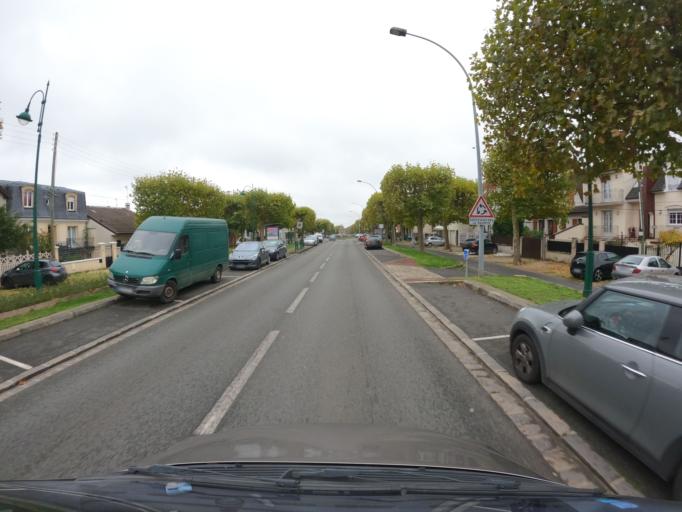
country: FR
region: Ile-de-France
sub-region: Departement du Val-de-Marne
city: Chennevieres-sur-Marne
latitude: 48.7894
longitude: 2.5353
